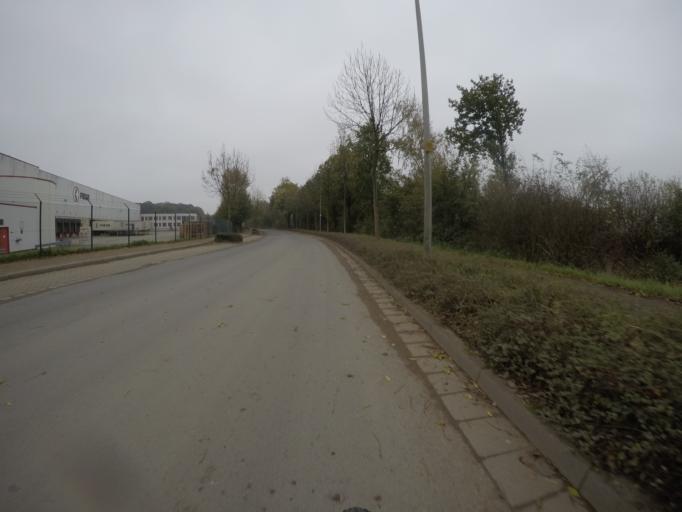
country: DE
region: North Rhine-Westphalia
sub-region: Regierungsbezirk Dusseldorf
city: Bocholt
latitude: 51.8087
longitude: 6.5453
